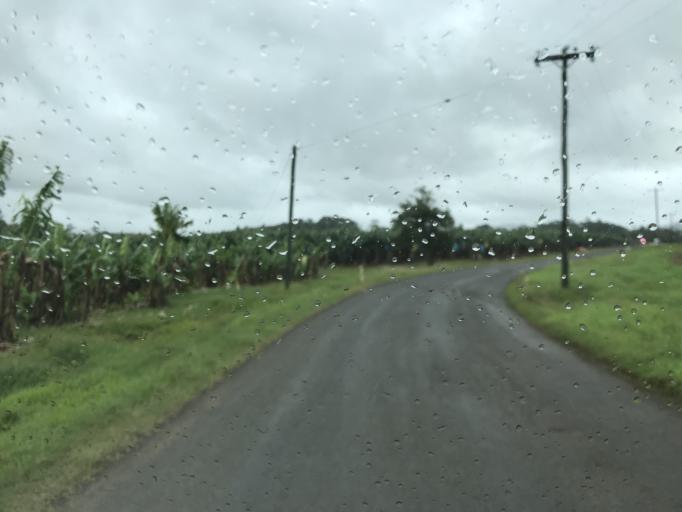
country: AU
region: Queensland
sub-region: Cassowary Coast
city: Innisfail
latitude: -17.5050
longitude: 145.9795
